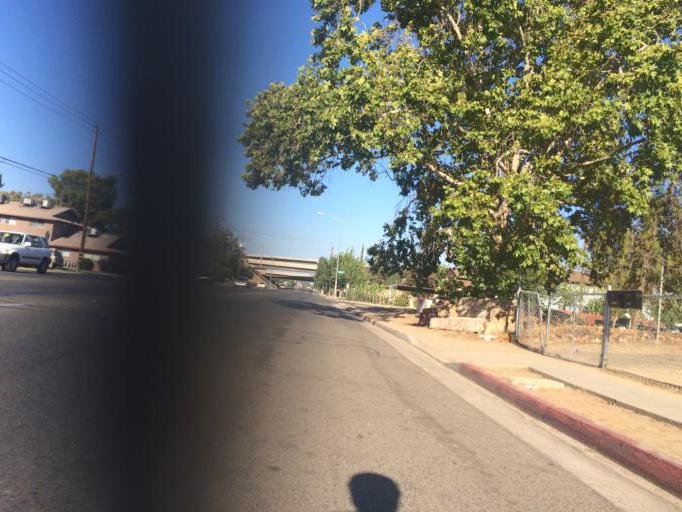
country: US
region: California
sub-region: Fresno County
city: Fresno
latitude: 36.7577
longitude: -119.7530
